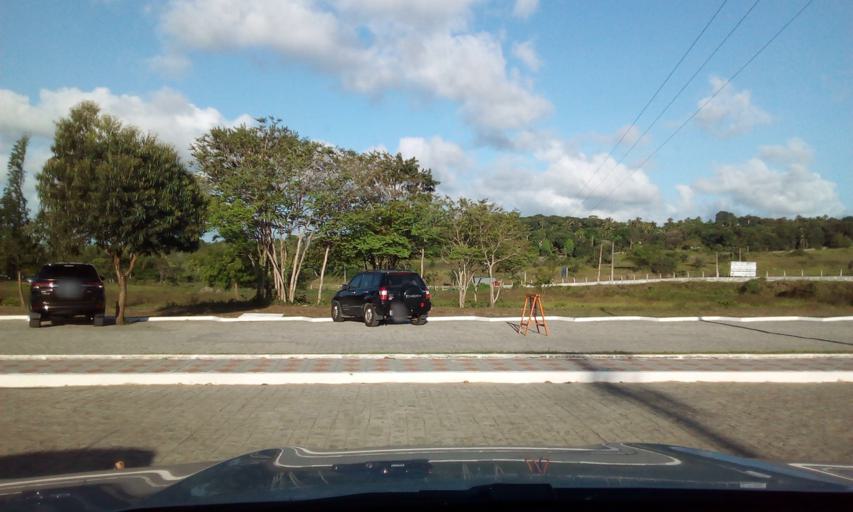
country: BR
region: Paraiba
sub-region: Conde
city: Conde
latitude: -7.2247
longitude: -34.9175
